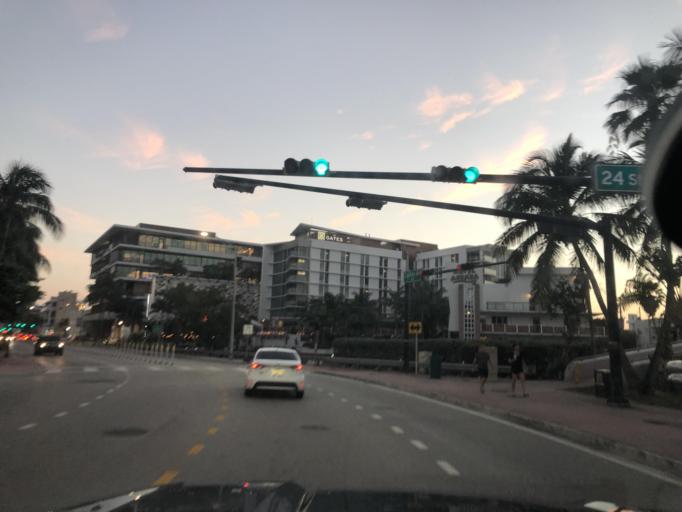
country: US
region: Florida
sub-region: Miami-Dade County
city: Miami Beach
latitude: 25.8004
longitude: -80.1271
